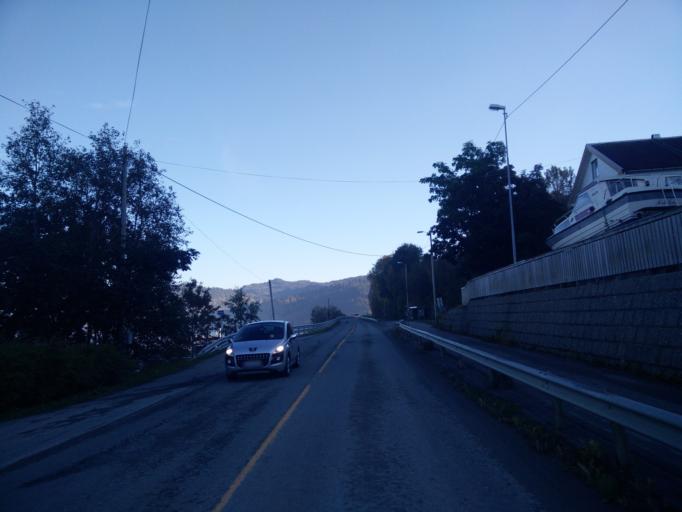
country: NO
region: Sor-Trondelag
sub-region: Skaun
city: Borsa
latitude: 63.3350
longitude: 10.0649
